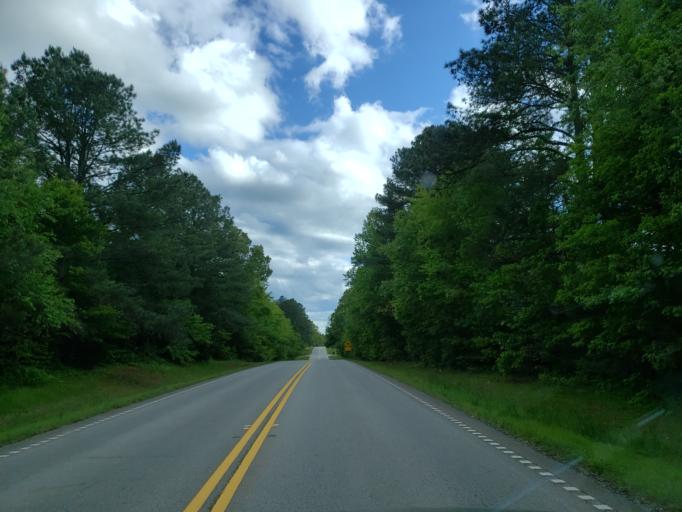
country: US
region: Georgia
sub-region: Haralson County
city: Tallapoosa
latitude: 33.8470
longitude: -85.2922
